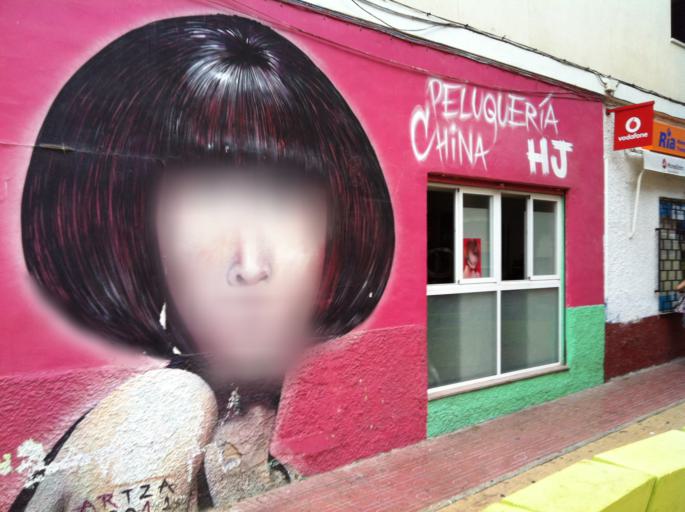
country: ES
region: Valencia
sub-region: Provincia de Alicante
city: Torrevieja
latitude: 37.9790
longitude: -0.6759
